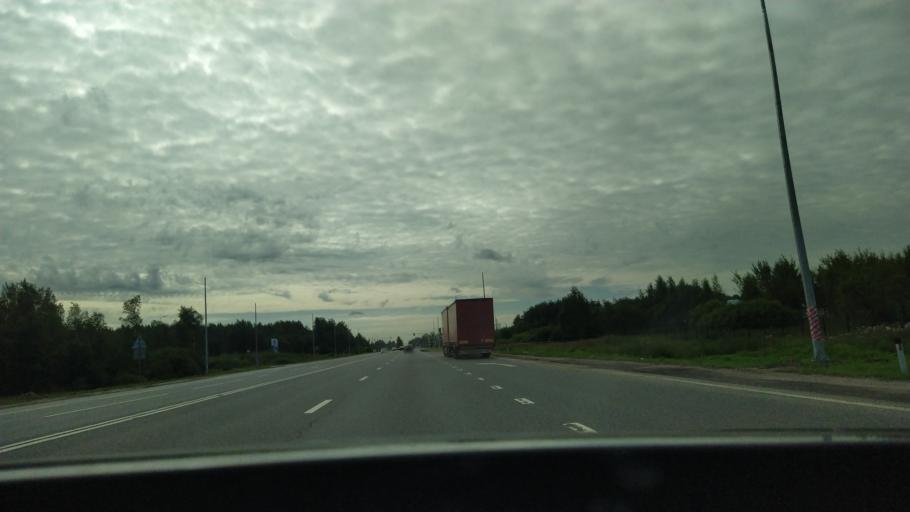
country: RU
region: Leningrad
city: Tosno
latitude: 59.5708
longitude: 30.8227
